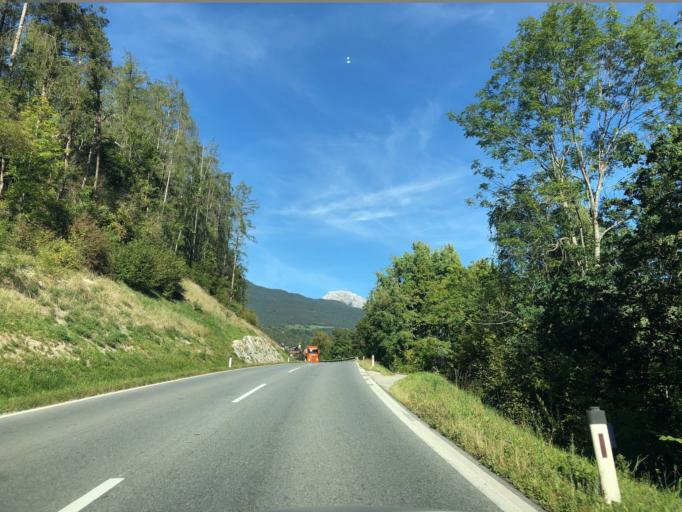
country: AT
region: Tyrol
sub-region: Politischer Bezirk Imst
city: Imst
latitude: 47.2561
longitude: 10.7516
